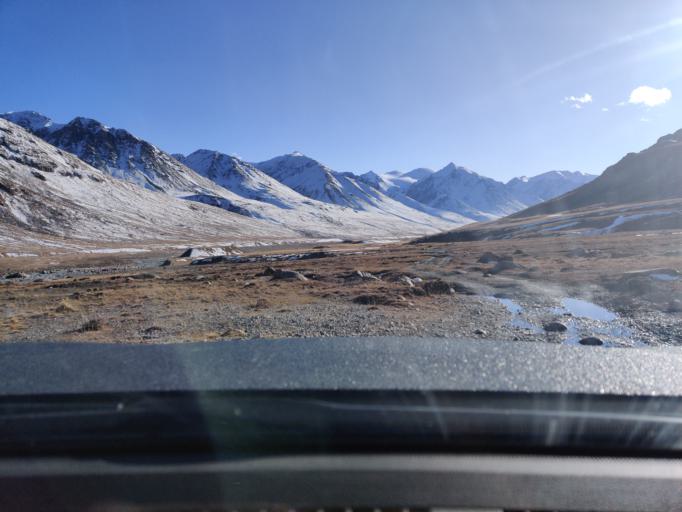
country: KG
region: Ysyk-Koel
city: Kadzhi-Say
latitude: 41.8107
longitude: 77.5761
